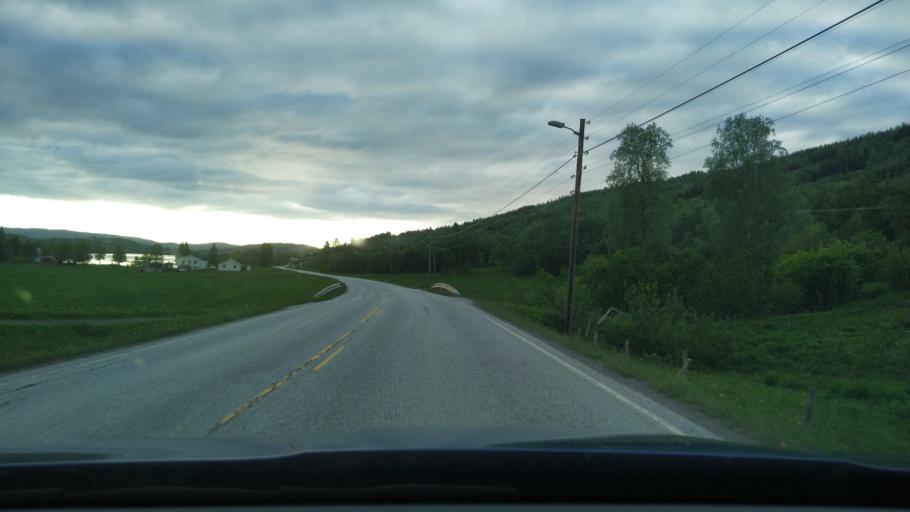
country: NO
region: Troms
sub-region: Sorreisa
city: Sorreisa
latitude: 69.1265
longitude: 18.2130
